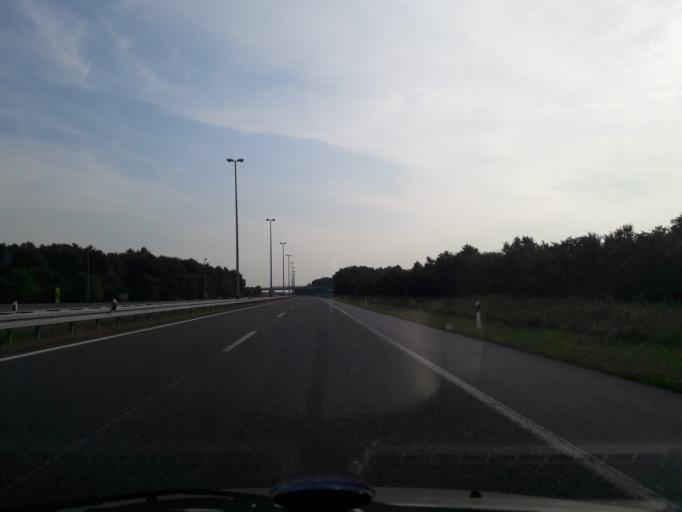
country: HR
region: Osjecko-Baranjska
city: Vuka
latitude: 45.4752
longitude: 18.4856
